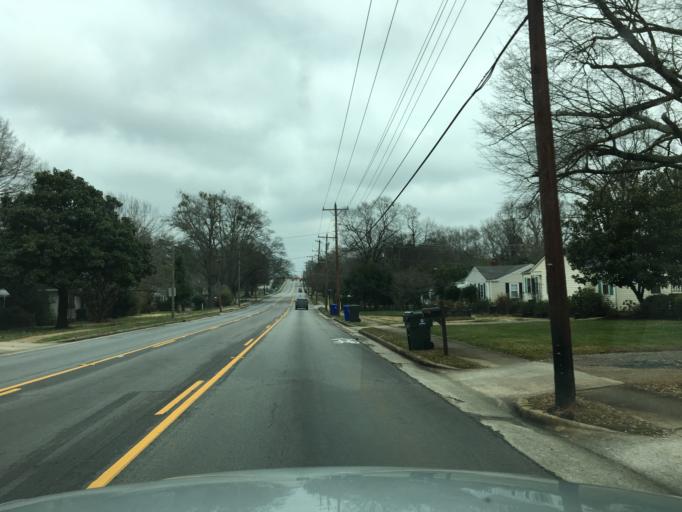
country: US
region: South Carolina
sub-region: Greenville County
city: Greenville
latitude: 34.8650
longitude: -82.3651
